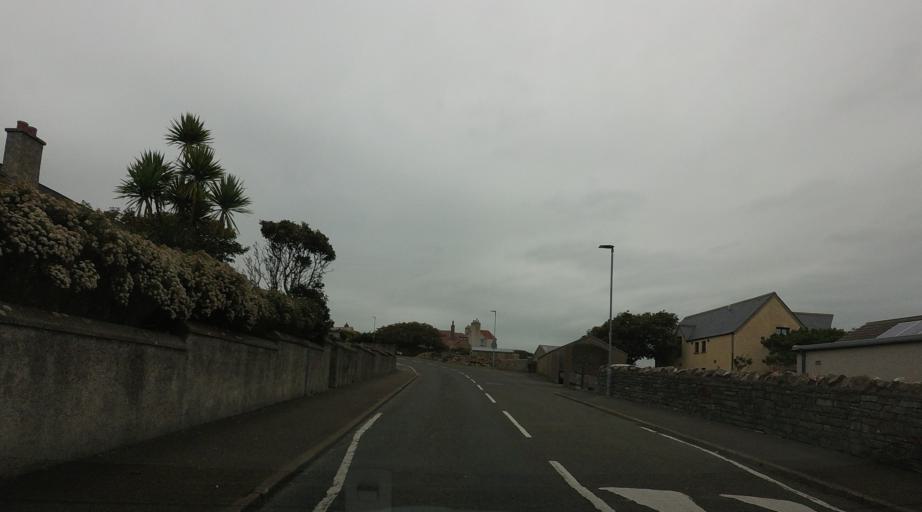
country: GB
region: Scotland
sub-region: Orkney Islands
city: Stromness
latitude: 58.9555
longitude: -3.3020
